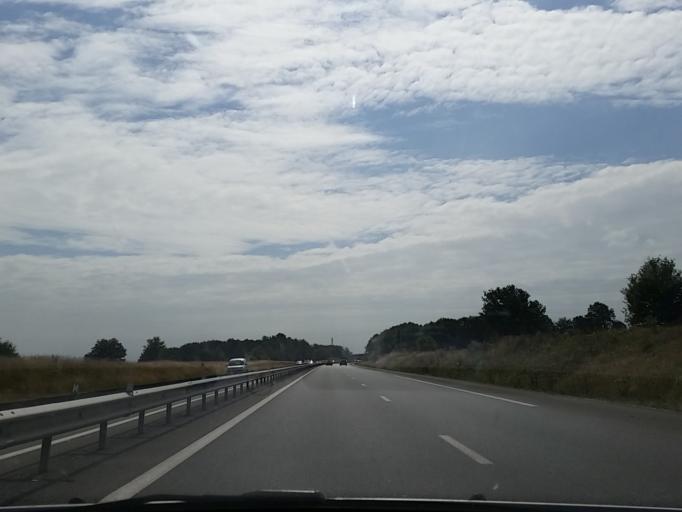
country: FR
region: Auvergne
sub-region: Departement de l'Allier
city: Vallon-en-Sully
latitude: 46.5258
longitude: 2.5680
